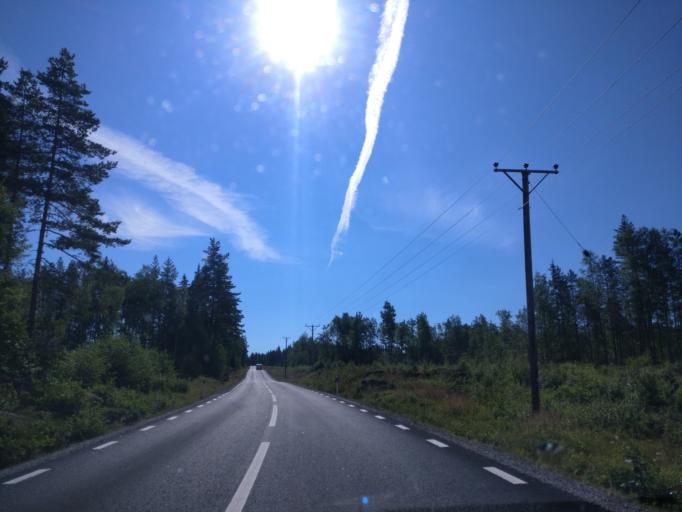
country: SE
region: Vaermland
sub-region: Hagfors Kommun
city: Hagfors
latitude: 60.0252
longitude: 13.8777
